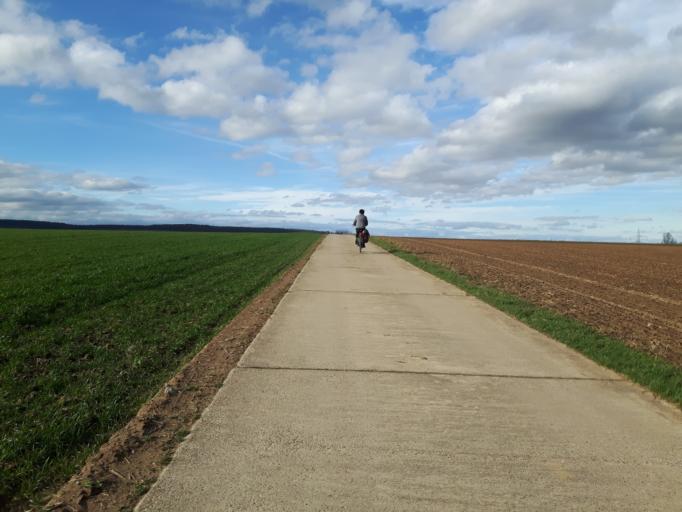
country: DE
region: Baden-Wuerttemberg
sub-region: Regierungsbezirk Stuttgart
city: Nordheim
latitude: 49.0950
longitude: 9.1145
